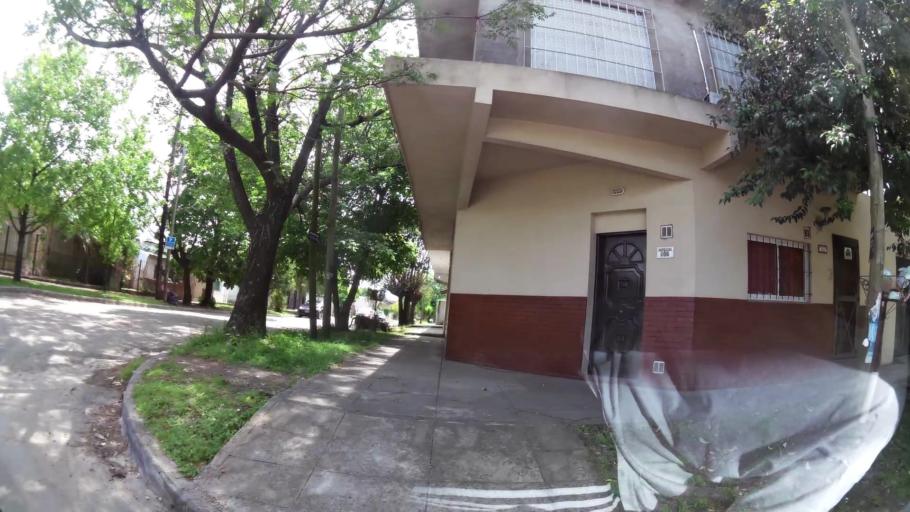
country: AR
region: Buenos Aires
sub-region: Partido de Quilmes
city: Quilmes
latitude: -34.7802
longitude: -58.2725
